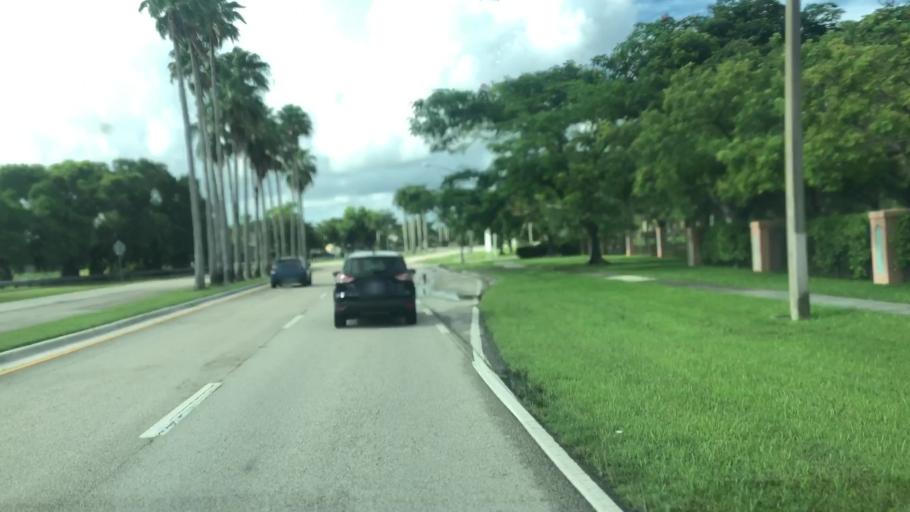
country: US
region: Florida
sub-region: Broward County
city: Tamarac
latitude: 26.1782
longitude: -80.2909
